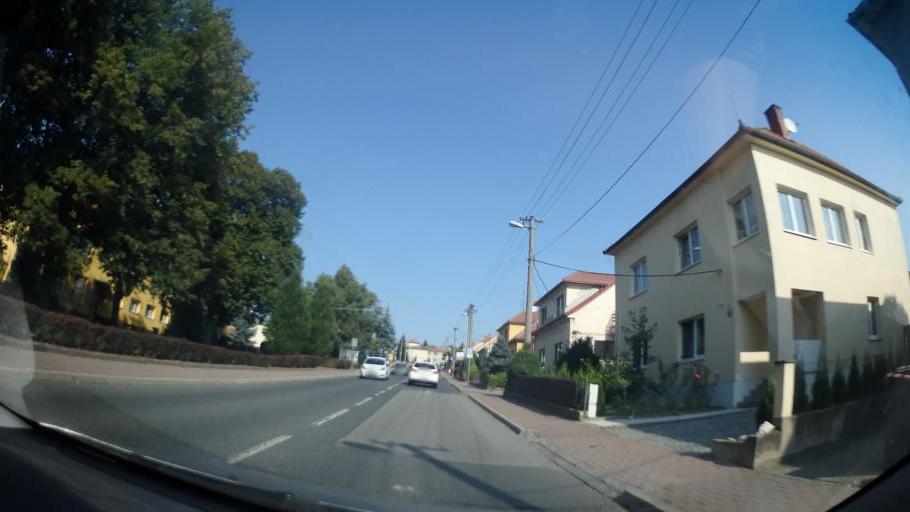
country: CZ
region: South Moravian
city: Kurim
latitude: 49.2356
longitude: 16.5282
